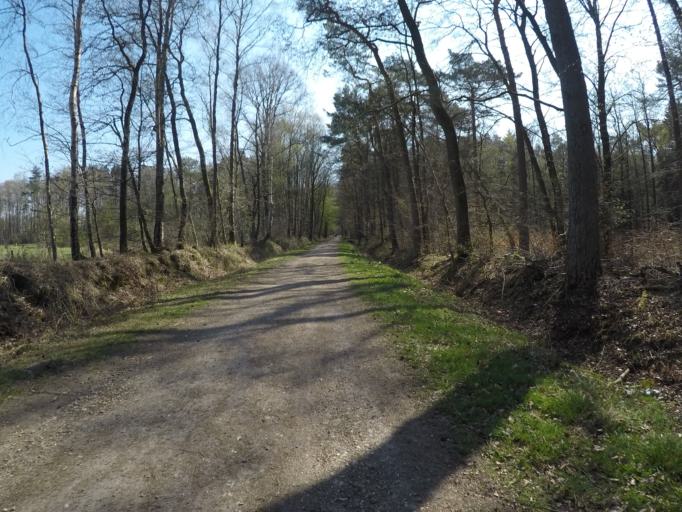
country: DE
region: Schleswig-Holstein
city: Rellingen
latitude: 53.6137
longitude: 9.7788
